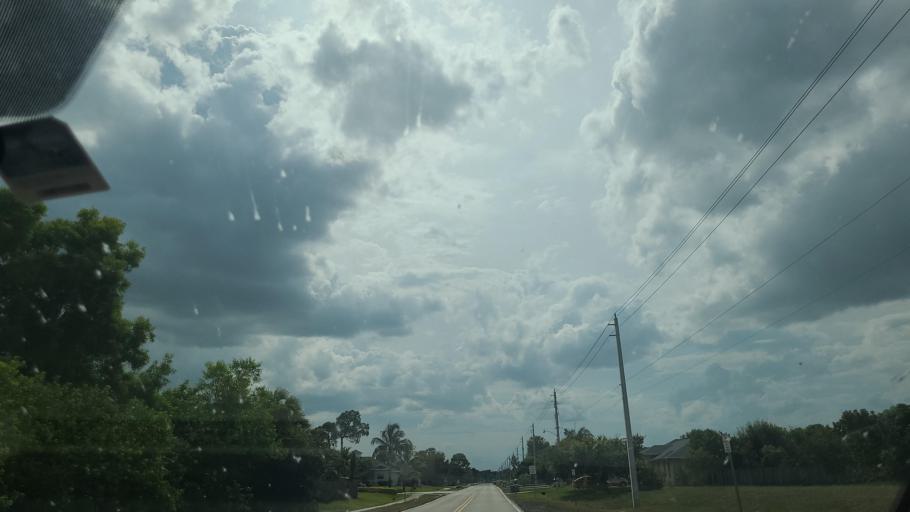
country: US
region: Florida
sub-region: Saint Lucie County
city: Port Saint Lucie
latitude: 27.2425
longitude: -80.3657
